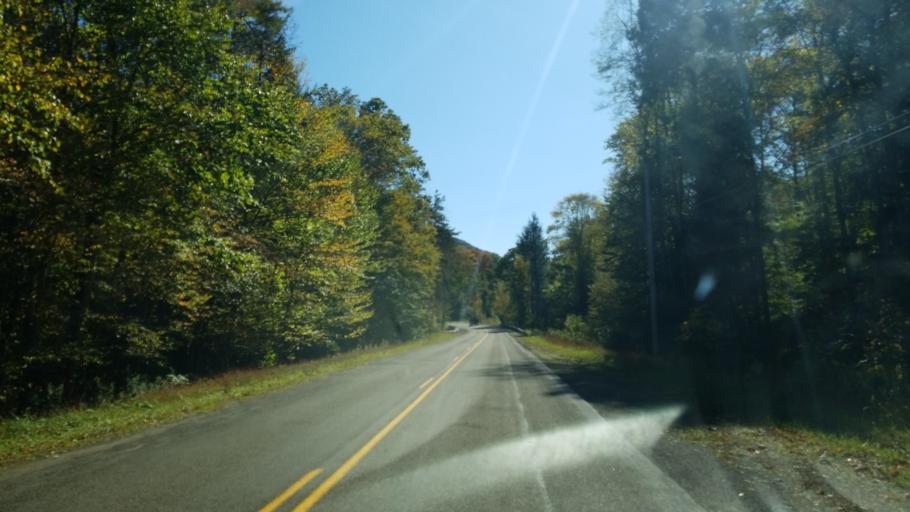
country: US
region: Pennsylvania
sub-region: Elk County
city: Saint Marys
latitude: 41.2708
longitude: -78.4029
